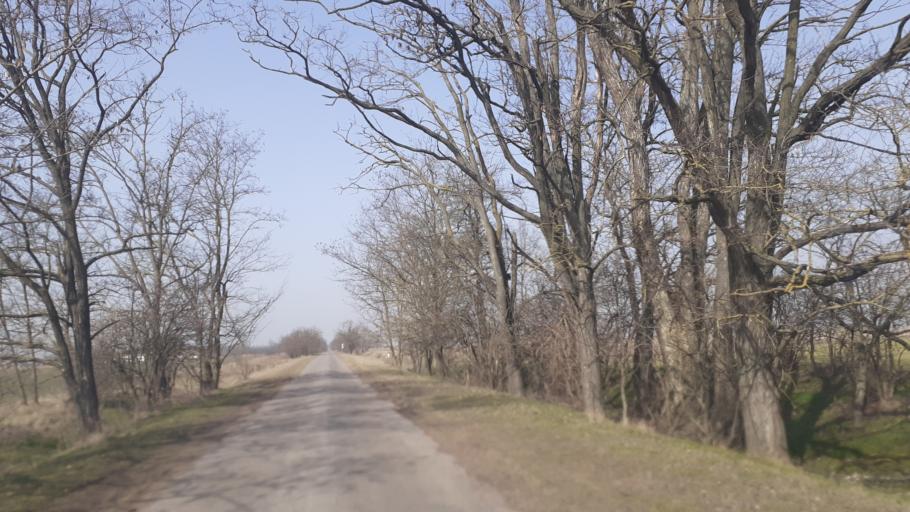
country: HU
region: Pest
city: Dabas
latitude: 47.0774
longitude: 19.2515
